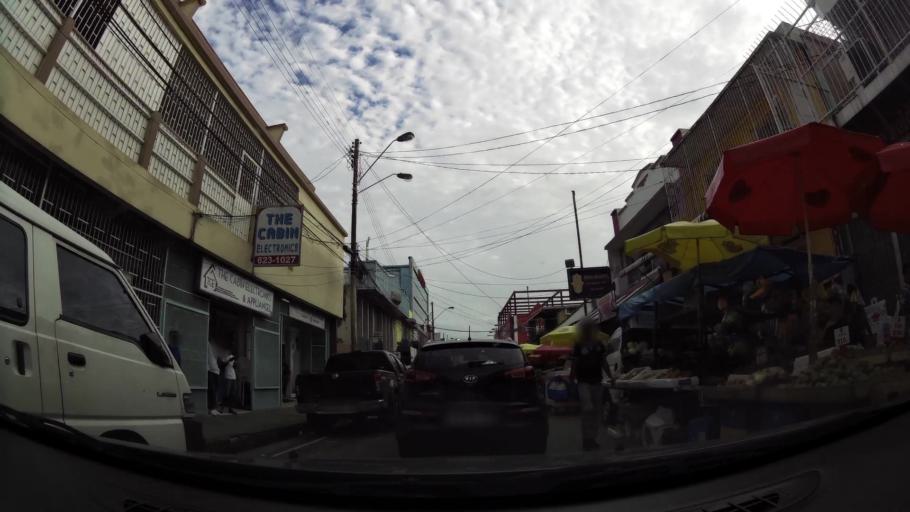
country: TT
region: San Juan/Laventille
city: Laventille
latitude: 10.6549
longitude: -61.5082
